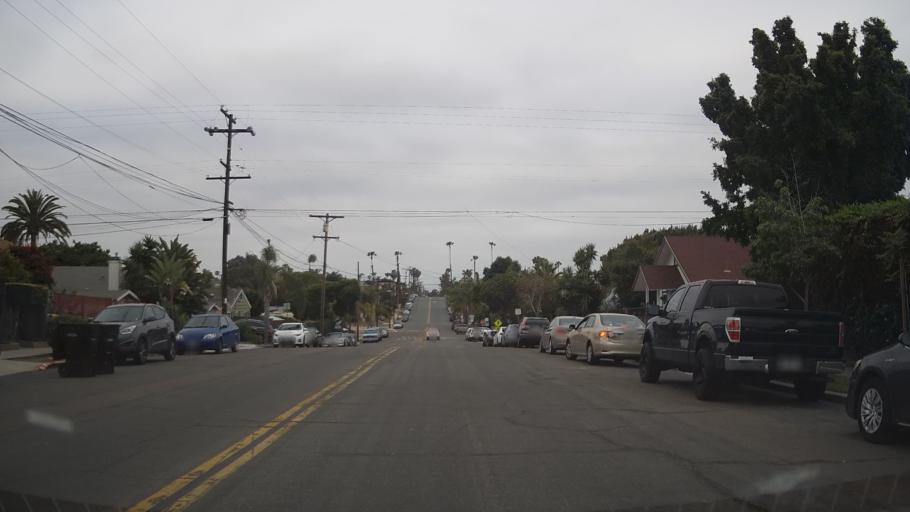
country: US
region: California
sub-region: San Diego County
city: San Diego
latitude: 32.7592
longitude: -117.1416
